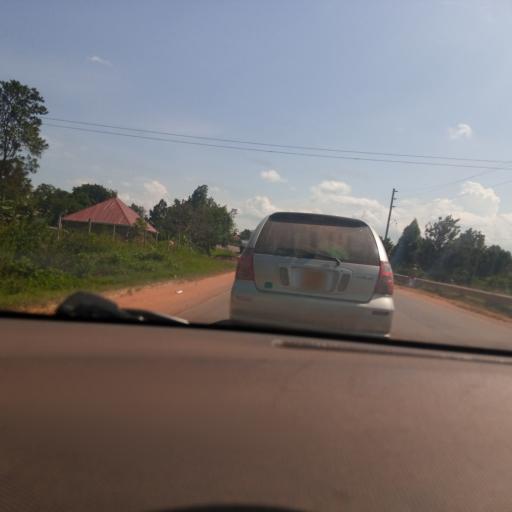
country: UG
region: Central Region
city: Masaka
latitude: -0.3139
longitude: 31.7448
